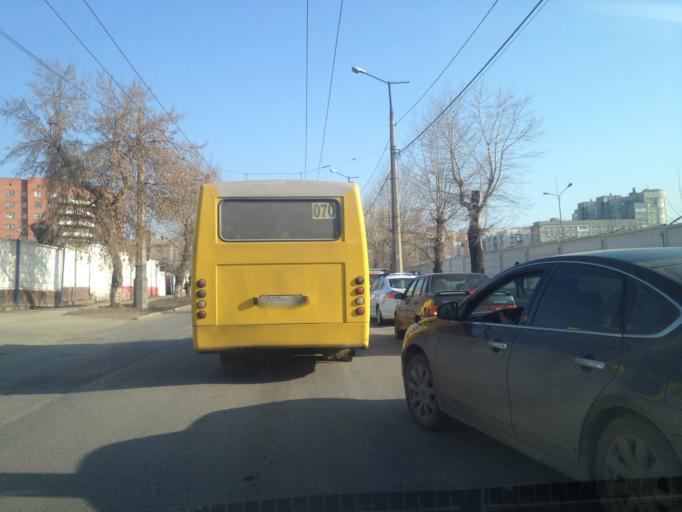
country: RU
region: Sverdlovsk
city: Yekaterinburg
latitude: 56.8267
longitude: 60.5672
